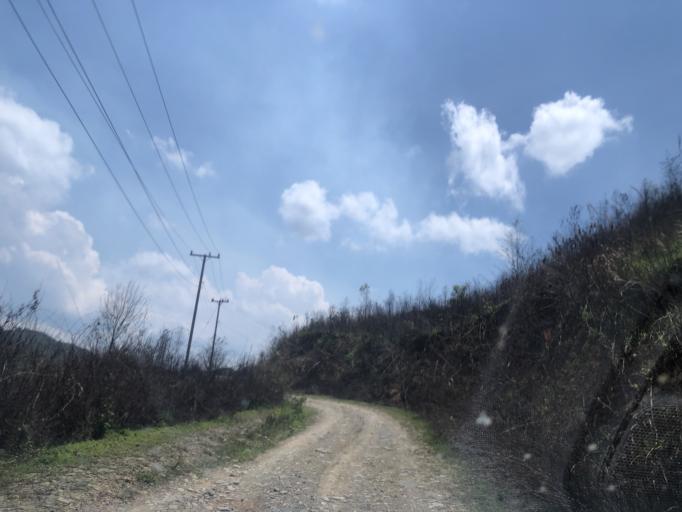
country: LA
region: Phongsali
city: Phongsali
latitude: 21.4099
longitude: 102.1869
